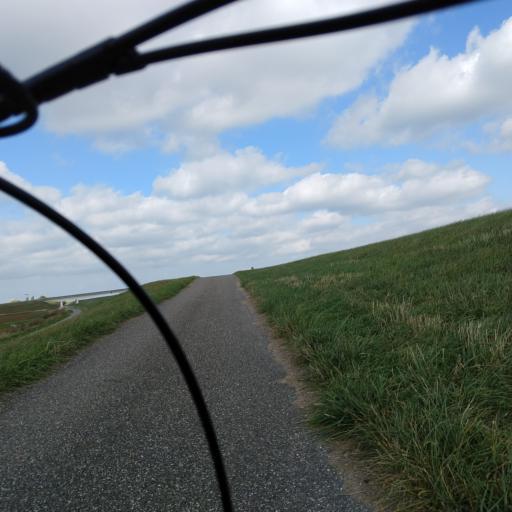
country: NL
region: Zeeland
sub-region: Gemeente Goes
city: Goes
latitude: 51.5922
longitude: 3.8727
